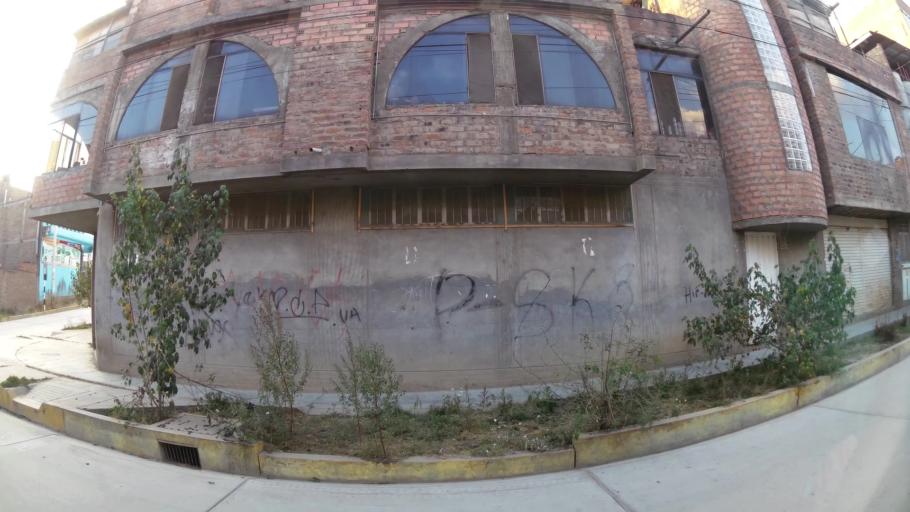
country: PE
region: Junin
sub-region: Provincia de Huancayo
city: Pilcomay
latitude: -12.0446
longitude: -75.2273
